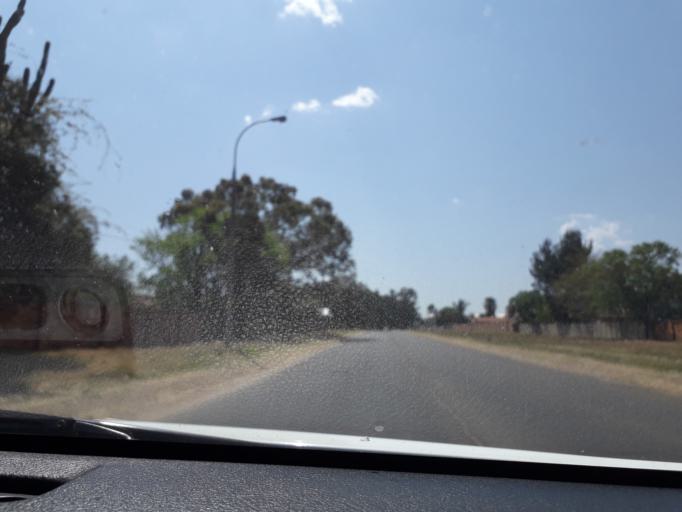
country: ZA
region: Gauteng
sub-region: City of Johannesburg Metropolitan Municipality
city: Modderfontein
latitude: -26.0850
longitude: 28.1999
